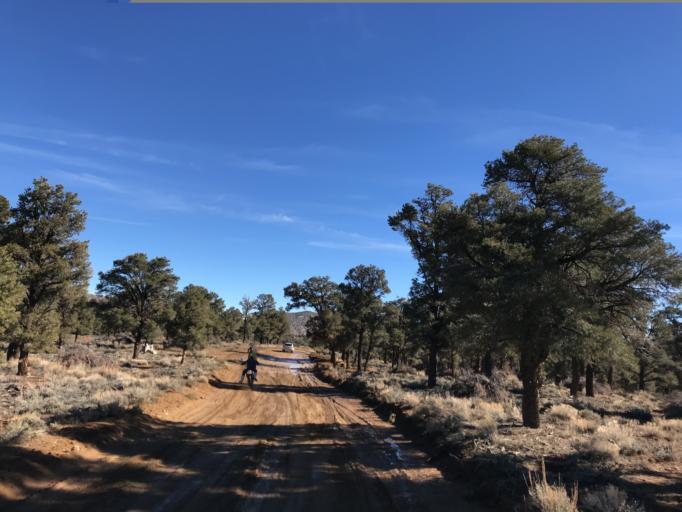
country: US
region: California
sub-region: San Bernardino County
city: Big Bear City
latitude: 34.2656
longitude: -116.7588
